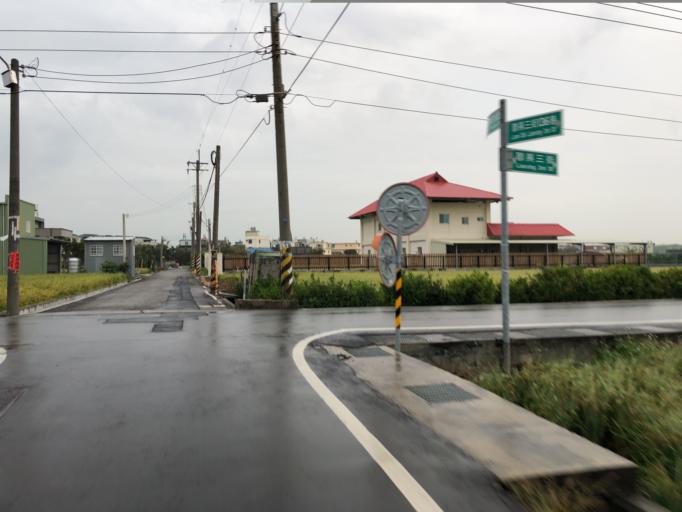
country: TW
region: Taiwan
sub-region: Hsinchu
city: Zhubei
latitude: 24.8505
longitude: 120.9900
